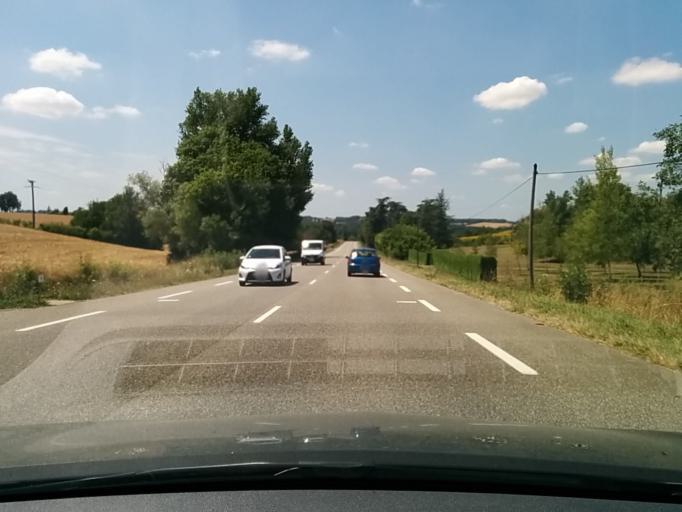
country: FR
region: Midi-Pyrenees
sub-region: Departement du Gers
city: Jegun
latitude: 43.7235
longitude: 0.3928
